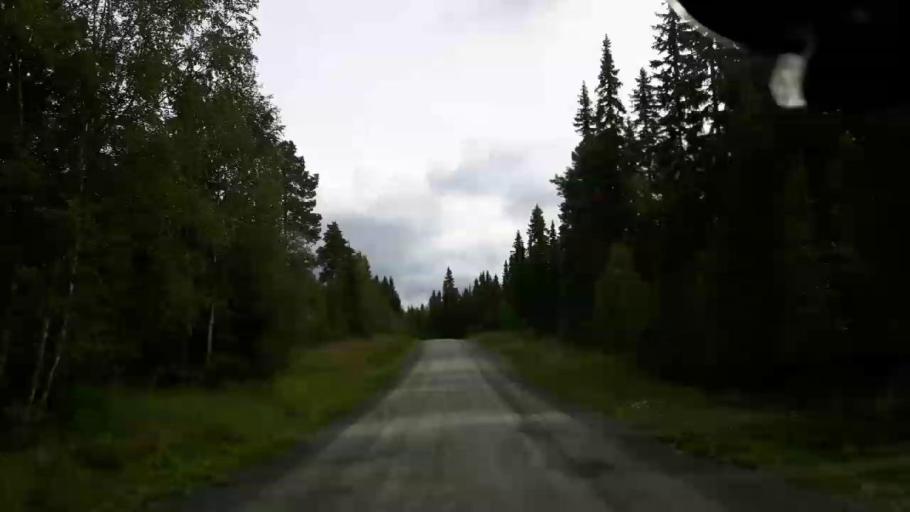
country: SE
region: Jaemtland
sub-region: Krokoms Kommun
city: Valla
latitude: 63.6386
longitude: 14.0074
